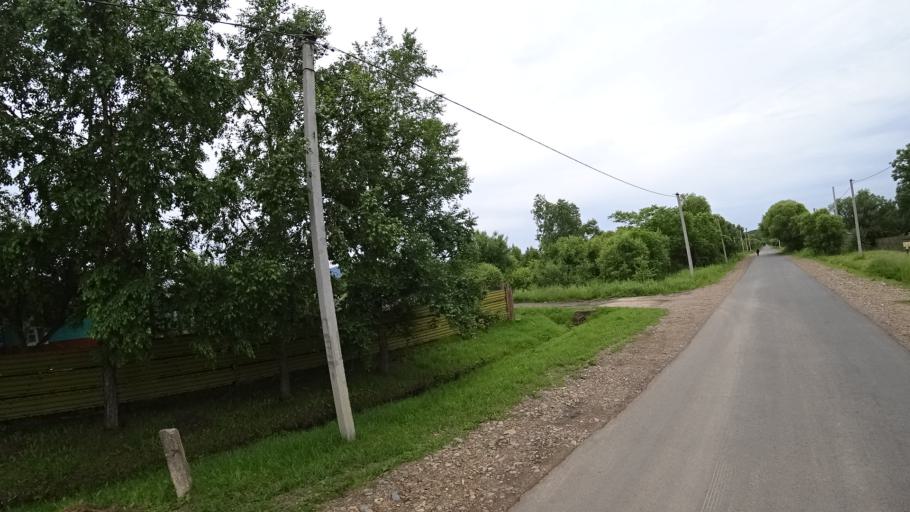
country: RU
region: Primorskiy
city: Novosysoyevka
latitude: 44.2091
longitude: 133.3345
